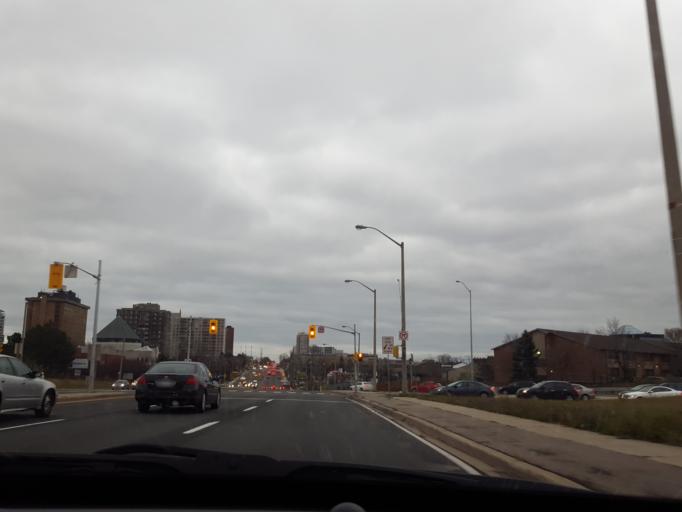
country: CA
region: Ontario
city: Scarborough
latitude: 43.7845
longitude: -79.2351
